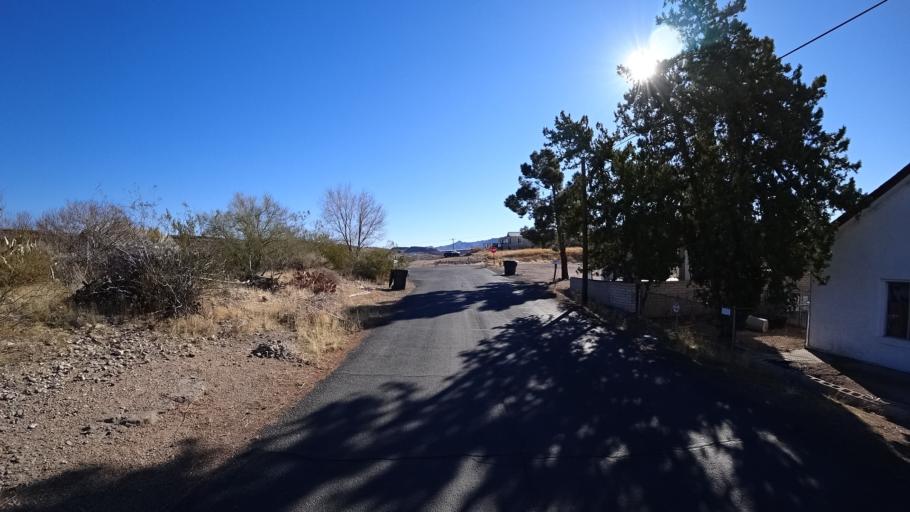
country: US
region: Arizona
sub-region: Mohave County
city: Kingman
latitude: 35.1870
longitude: -114.0571
